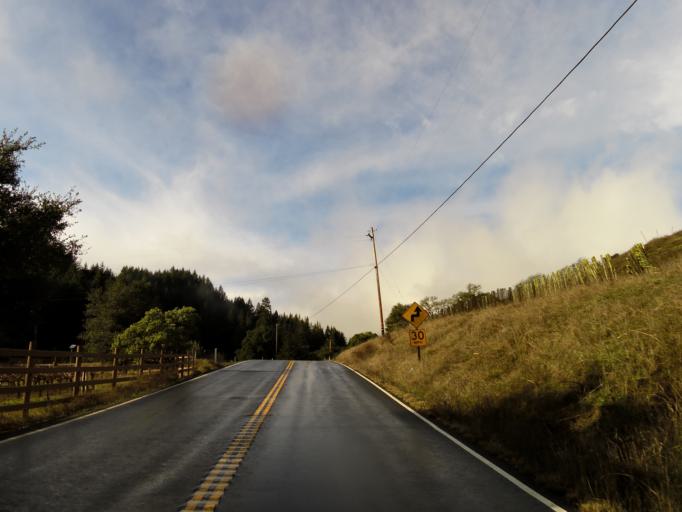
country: US
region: California
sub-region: Sonoma County
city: Cloverdale
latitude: 38.8802
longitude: -123.1139
